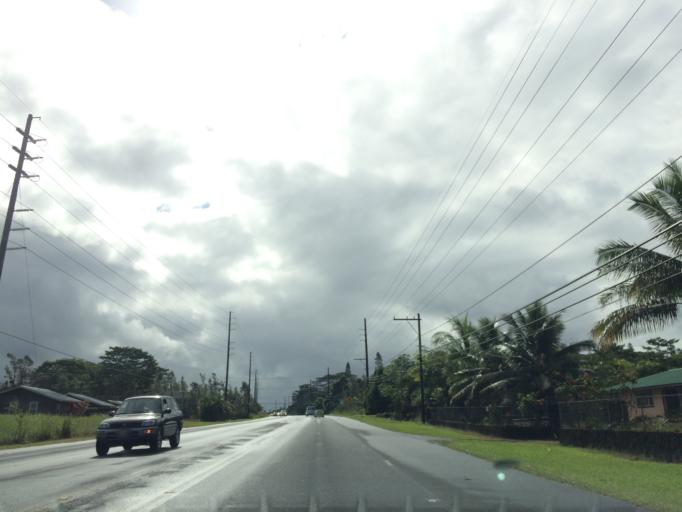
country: US
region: Hawaii
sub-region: Hawaii County
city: Orchidlands Estates
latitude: 19.5598
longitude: -154.9918
